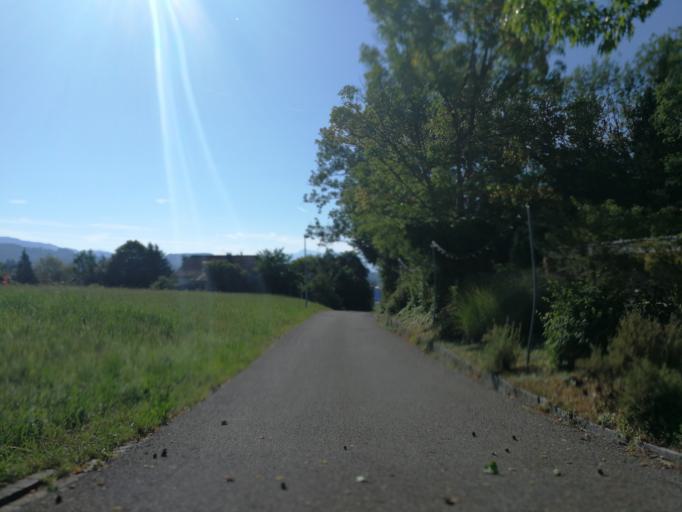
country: CH
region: Zurich
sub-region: Bezirk Hinwil
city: Bubikon
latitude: 47.2769
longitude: 8.8150
